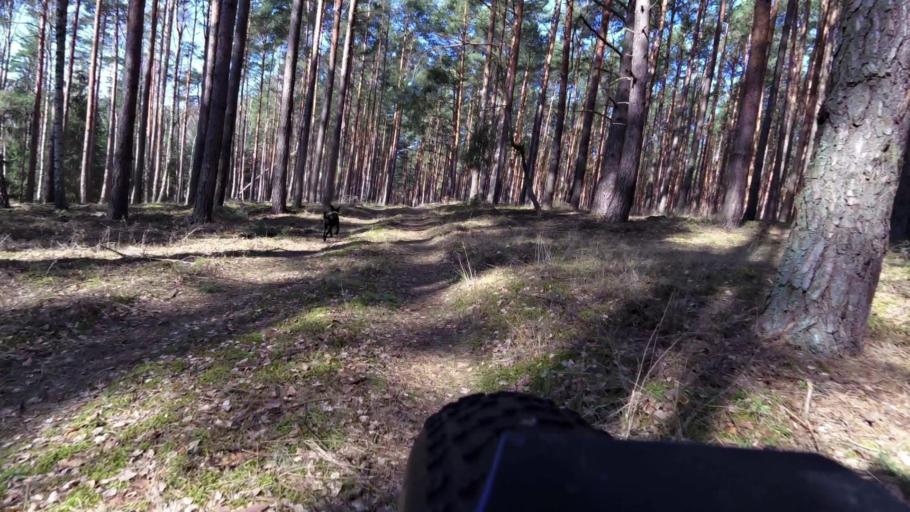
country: PL
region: Lubusz
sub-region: Powiat slubicki
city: Cybinka
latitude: 52.2090
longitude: 14.9239
